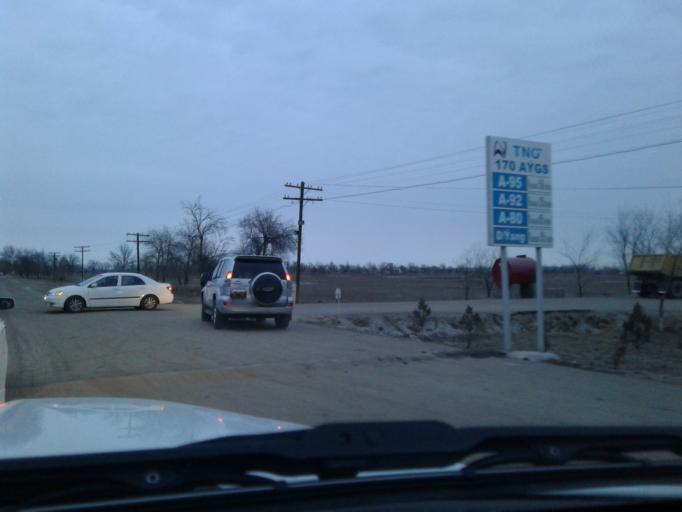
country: UZ
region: Karakalpakstan
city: Manghit
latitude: 42.0522
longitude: 59.9304
